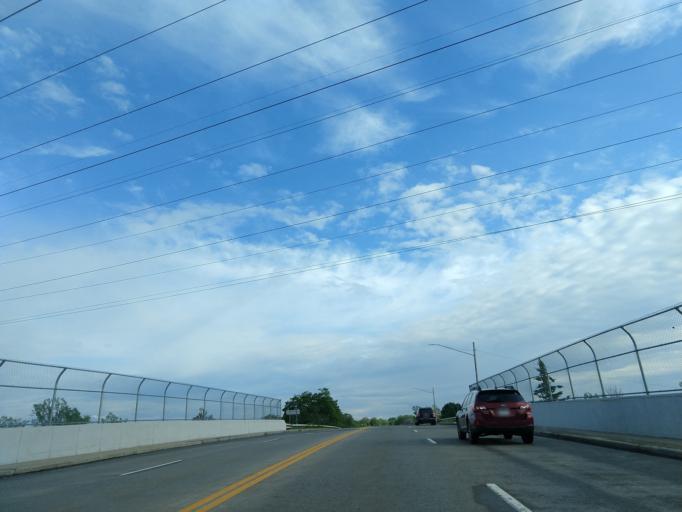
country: US
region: New York
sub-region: Erie County
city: West Seneca
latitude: 42.8548
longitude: -78.7878
